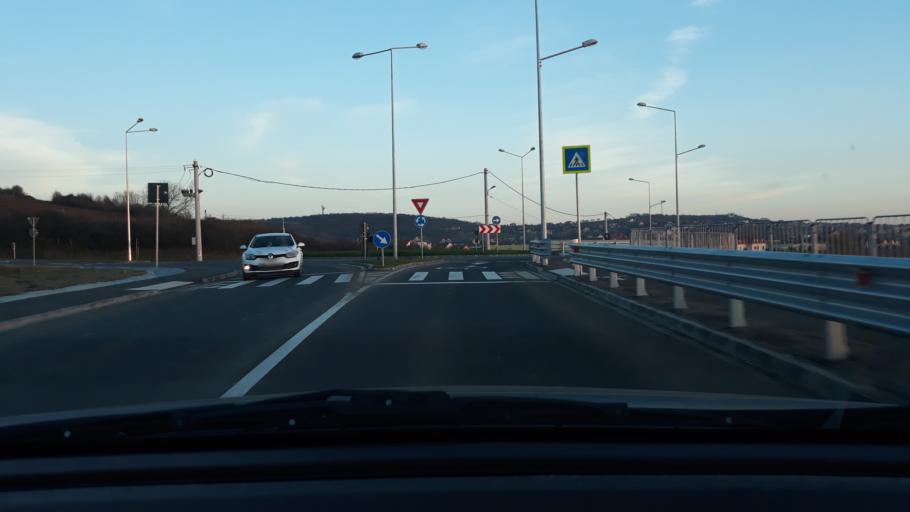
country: RO
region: Bihor
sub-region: Comuna Biharea
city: Oradea
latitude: 47.0970
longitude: 21.9218
